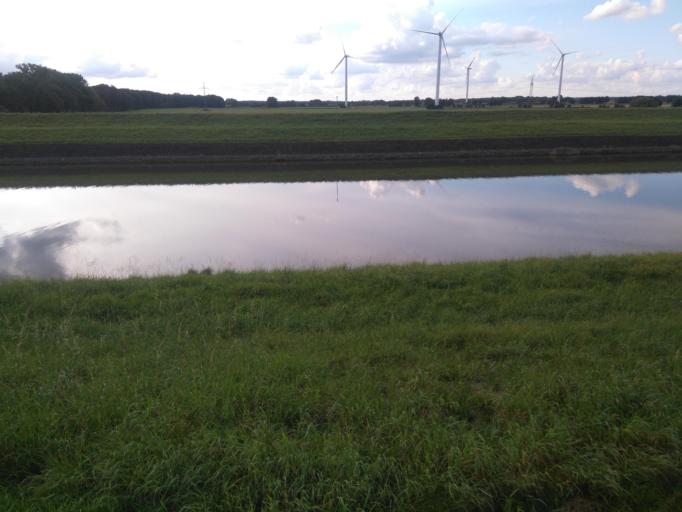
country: DE
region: Lower Saxony
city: Artlenburg
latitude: 53.3485
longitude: 10.5014
